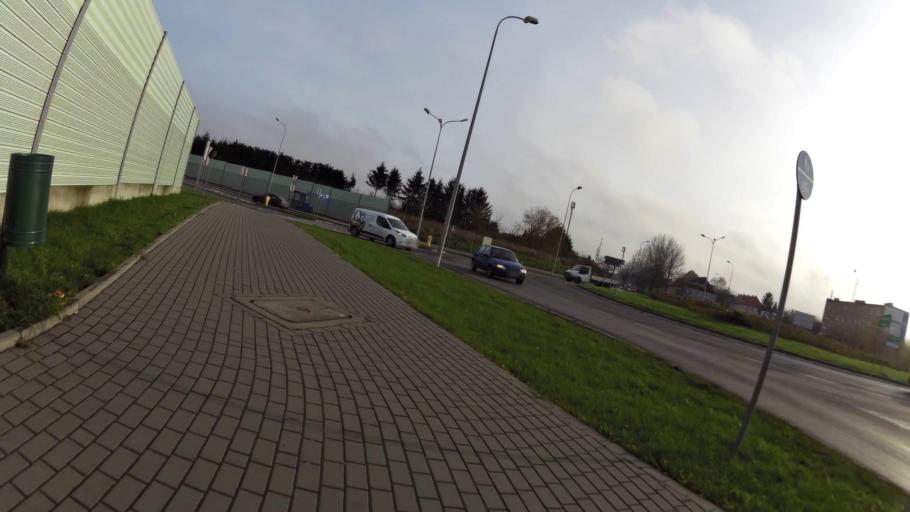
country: PL
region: West Pomeranian Voivodeship
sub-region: Koszalin
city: Koszalin
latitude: 54.2065
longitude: 16.1559
